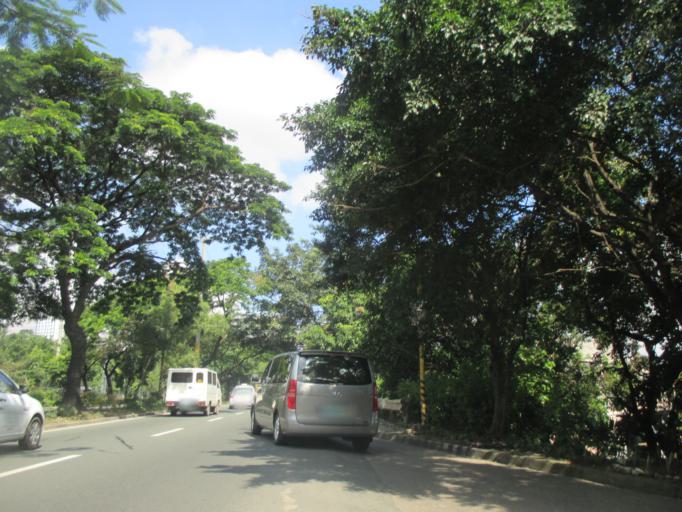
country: PH
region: Metro Manila
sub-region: Marikina
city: Calumpang
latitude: 14.6292
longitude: 121.0800
